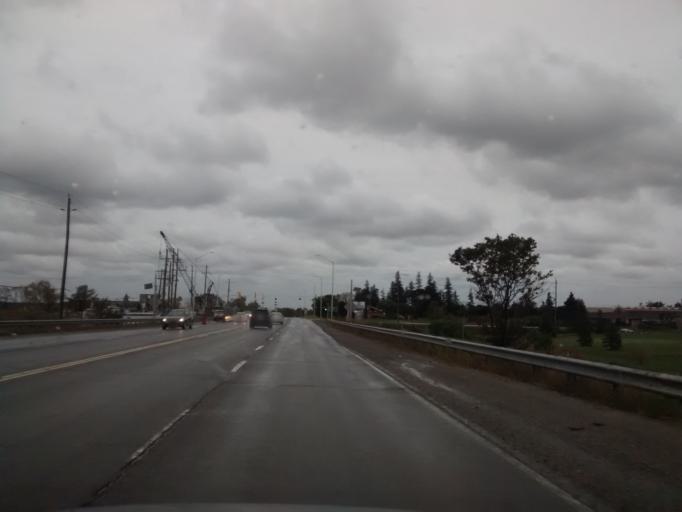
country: CA
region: Ontario
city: Hamilton
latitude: 43.1974
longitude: -79.7660
